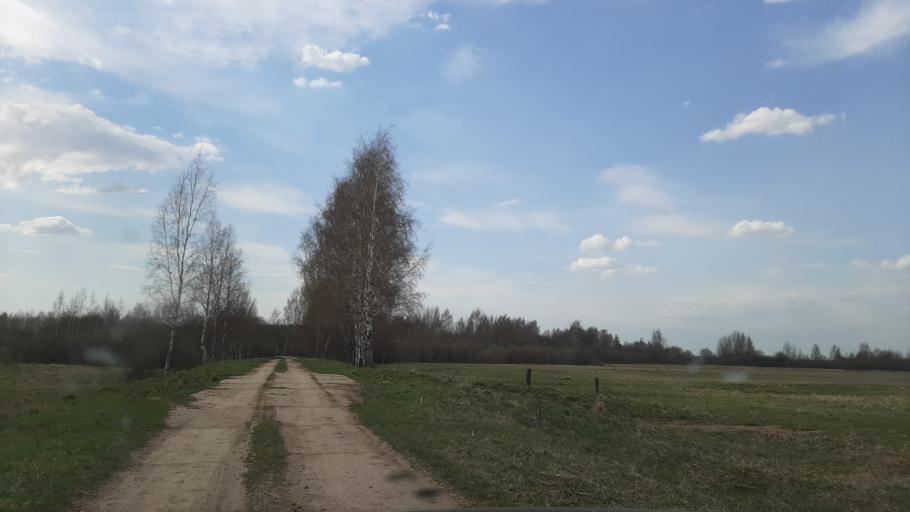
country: RU
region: Ivanovo
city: Privolzhsk
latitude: 57.3976
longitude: 41.3389
